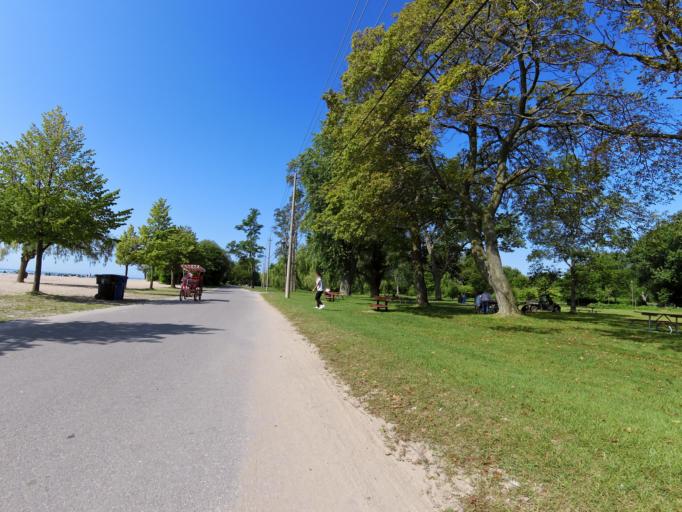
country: CA
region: Ontario
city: Toronto
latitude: 43.6159
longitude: -79.3747
